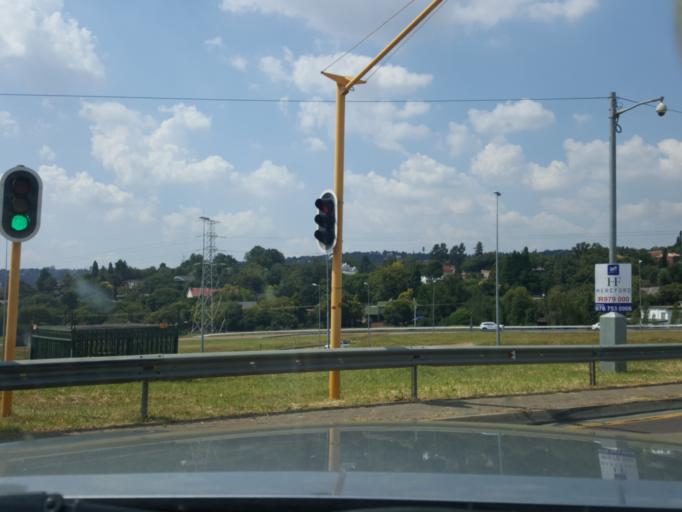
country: ZA
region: Gauteng
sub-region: City of Tshwane Metropolitan Municipality
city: Centurion
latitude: -25.8143
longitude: 28.2337
